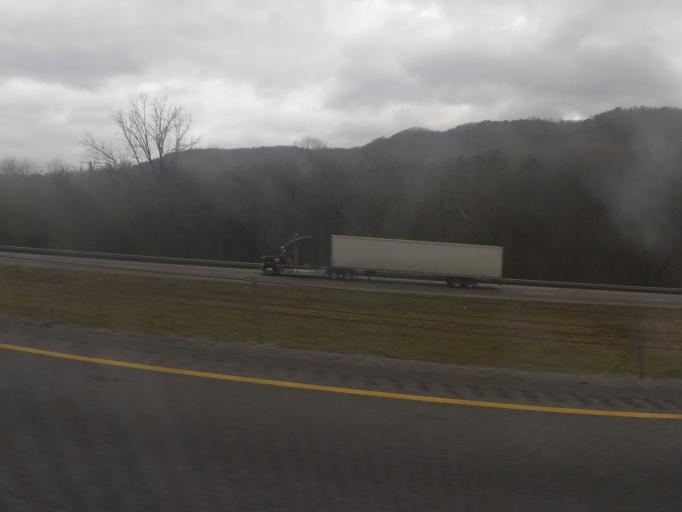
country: US
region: Tennessee
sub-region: Marion County
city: Jasper
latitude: 35.0115
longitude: -85.5321
